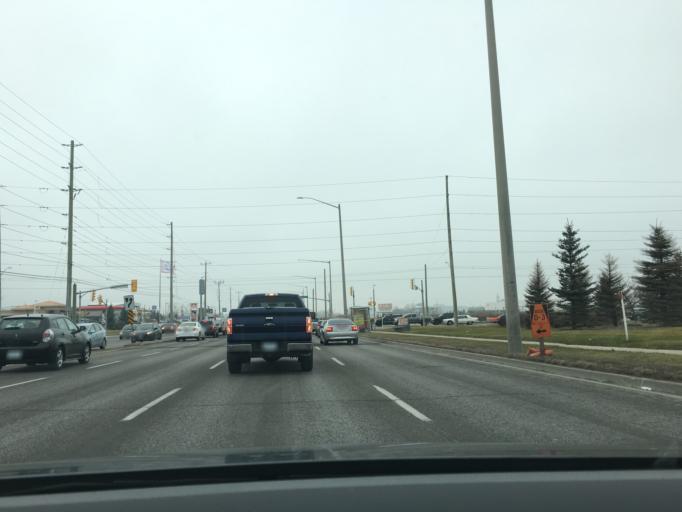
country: CA
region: Ontario
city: Innisfil
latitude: 44.3325
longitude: -79.6979
